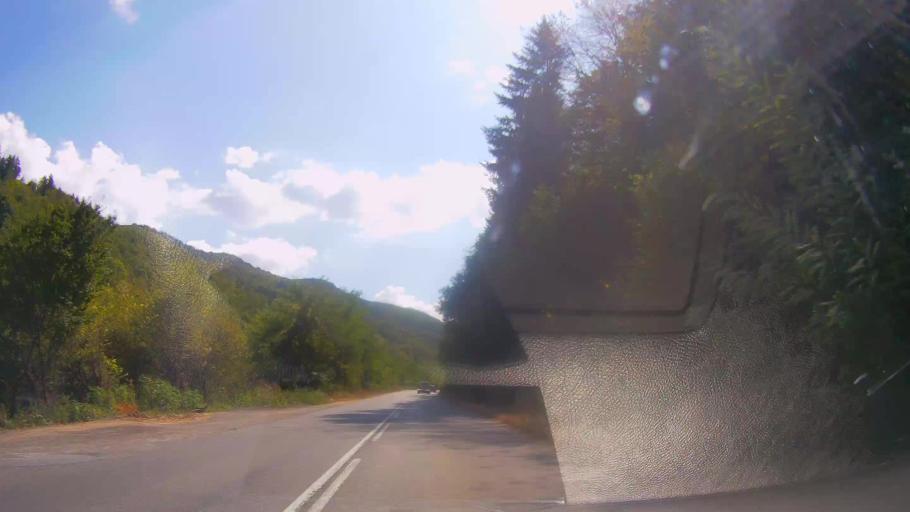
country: BG
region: Stara Zagora
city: Gurkovo
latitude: 42.7586
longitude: 25.7073
